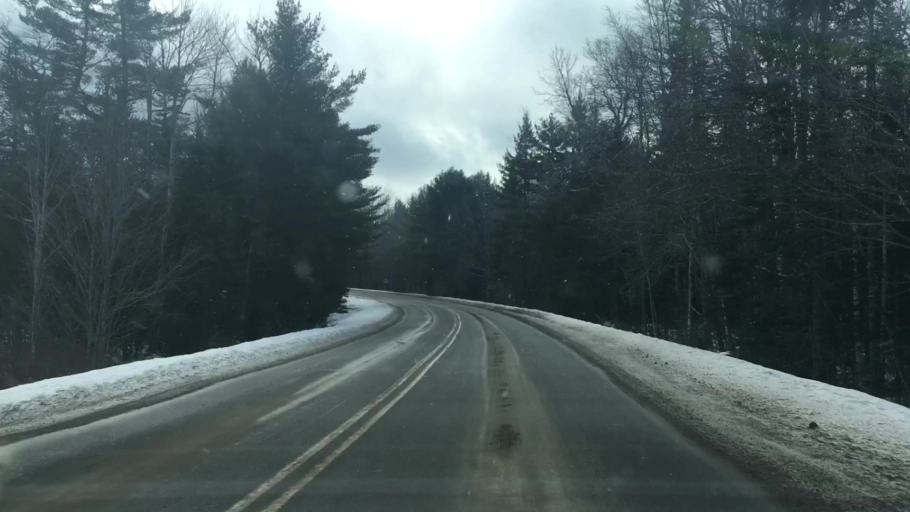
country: US
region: Maine
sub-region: Washington County
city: Calais
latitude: 45.0466
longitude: -67.3276
